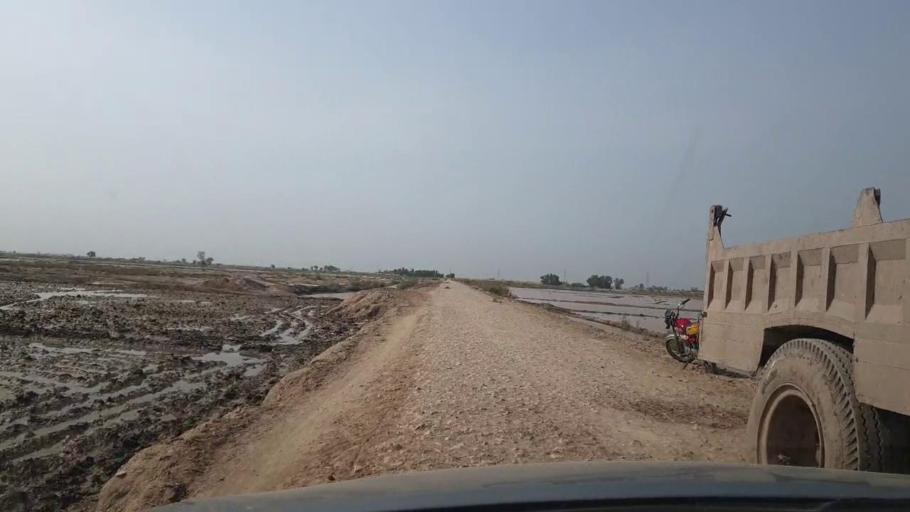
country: PK
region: Sindh
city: Lakhi
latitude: 27.8414
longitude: 68.6997
